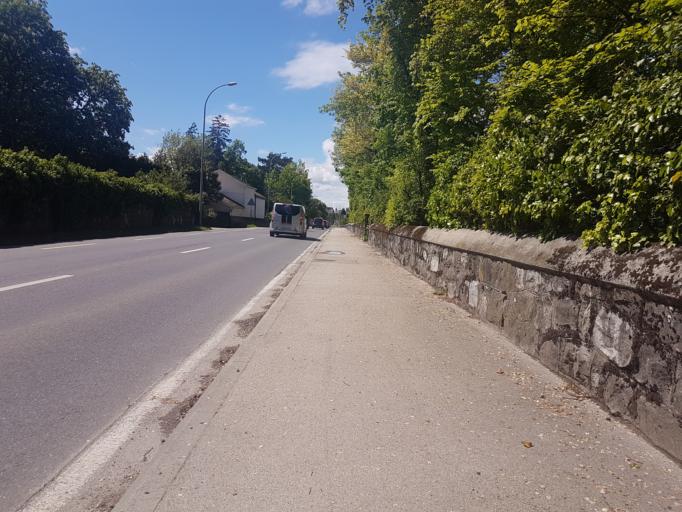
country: CH
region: Vaud
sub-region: Nyon District
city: Prangins
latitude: 46.3920
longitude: 6.2531
